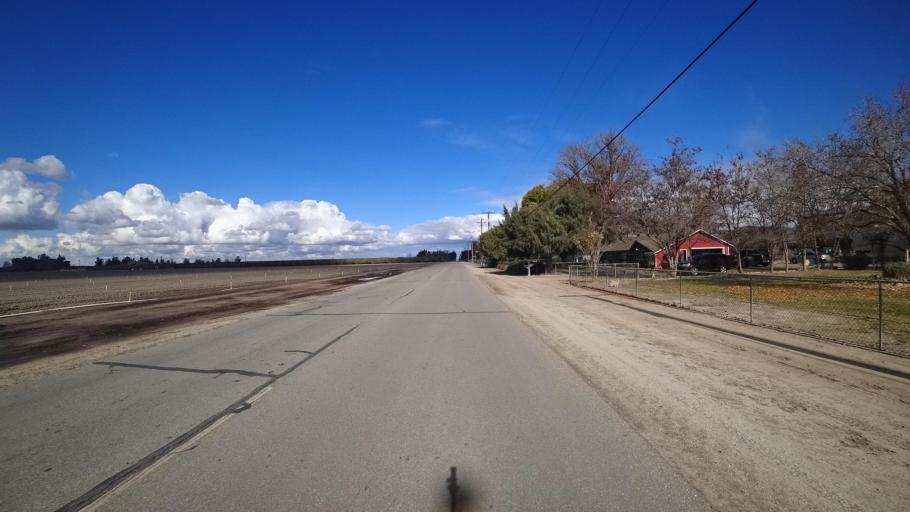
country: US
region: California
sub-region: Kern County
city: Greenfield
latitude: 35.2424
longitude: -119.0745
